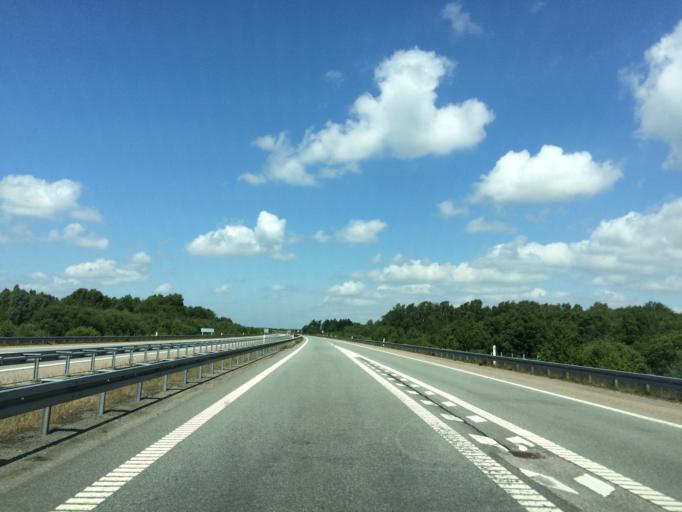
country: DK
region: Central Jutland
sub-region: Herning Kommune
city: Herning
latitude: 56.1599
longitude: 9.0066
